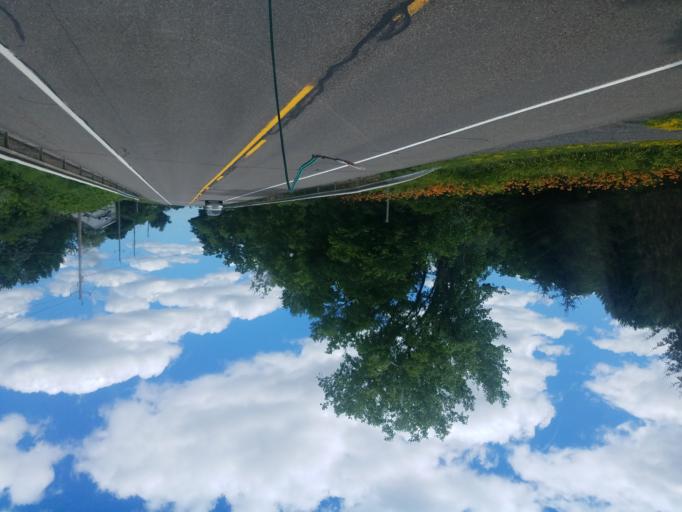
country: US
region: New York
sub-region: Ontario County
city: Phelps
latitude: 42.9685
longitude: -76.9775
